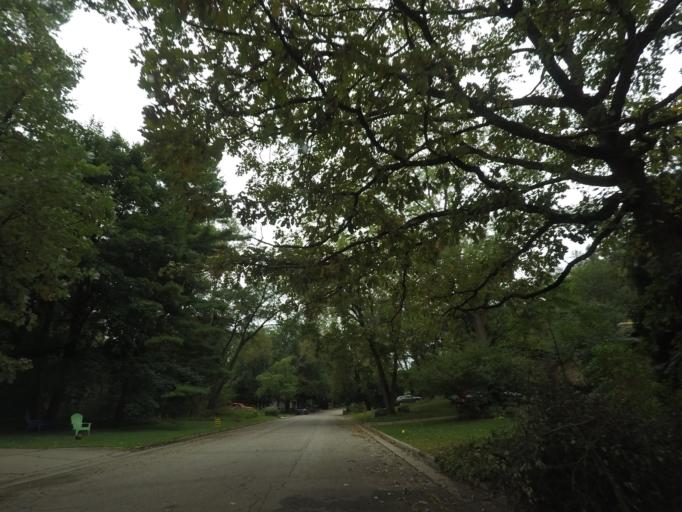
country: US
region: Wisconsin
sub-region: Dane County
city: Middleton
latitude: 43.0888
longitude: -89.4791
